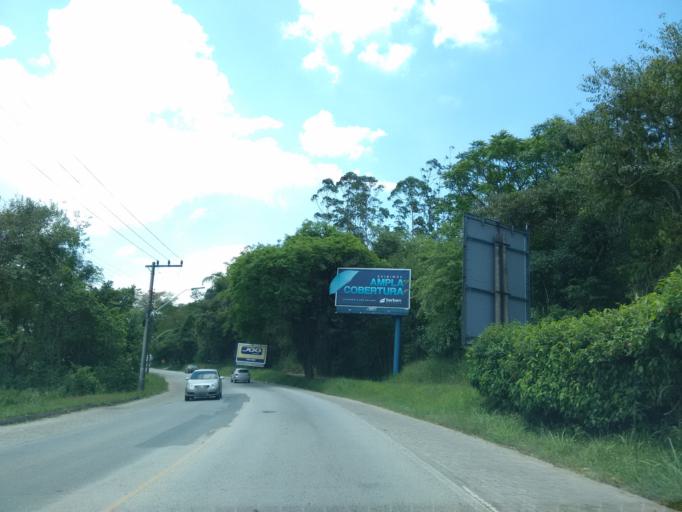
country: BR
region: Santa Catarina
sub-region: Blumenau
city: Blumenau
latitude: -26.9093
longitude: -49.0250
